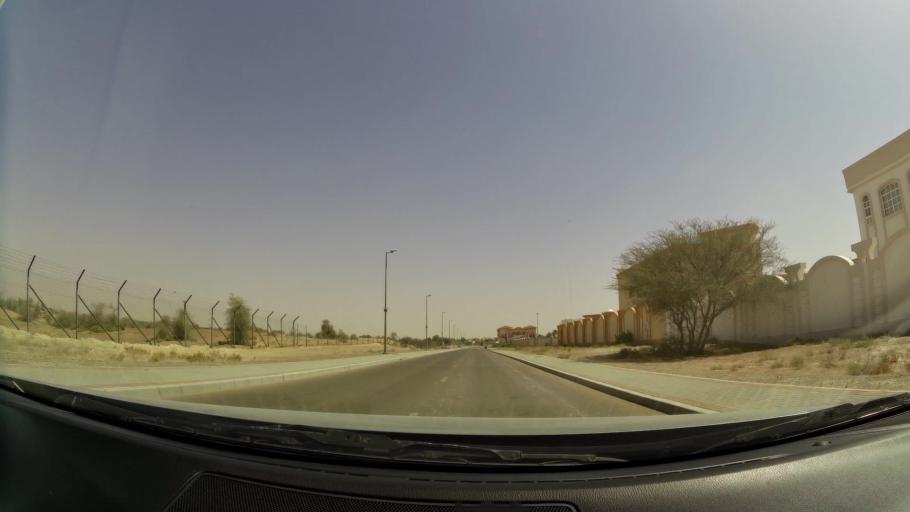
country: OM
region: Al Buraimi
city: Al Buraymi
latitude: 24.2903
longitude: 55.7581
